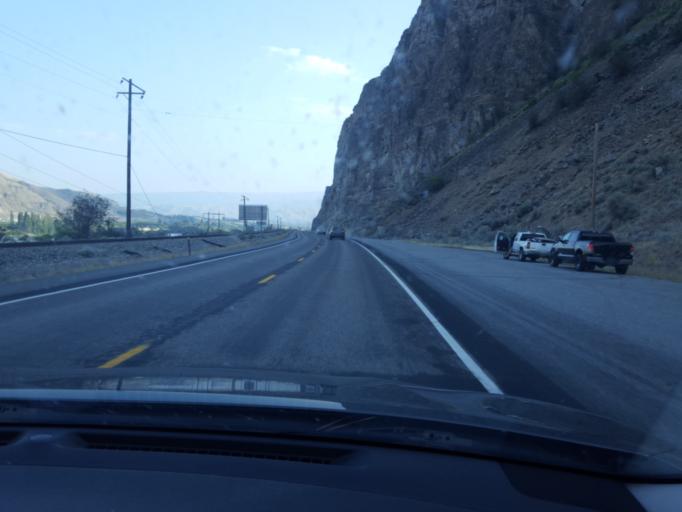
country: US
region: Washington
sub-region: Chelan County
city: Sunnyslope
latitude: 47.5202
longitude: -120.3070
